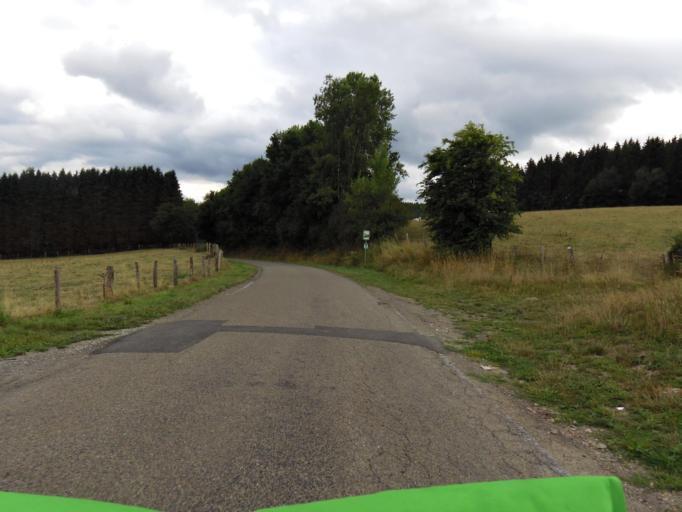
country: BE
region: Wallonia
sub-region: Province de Namur
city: Bievre
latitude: 49.9001
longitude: 5.0030
